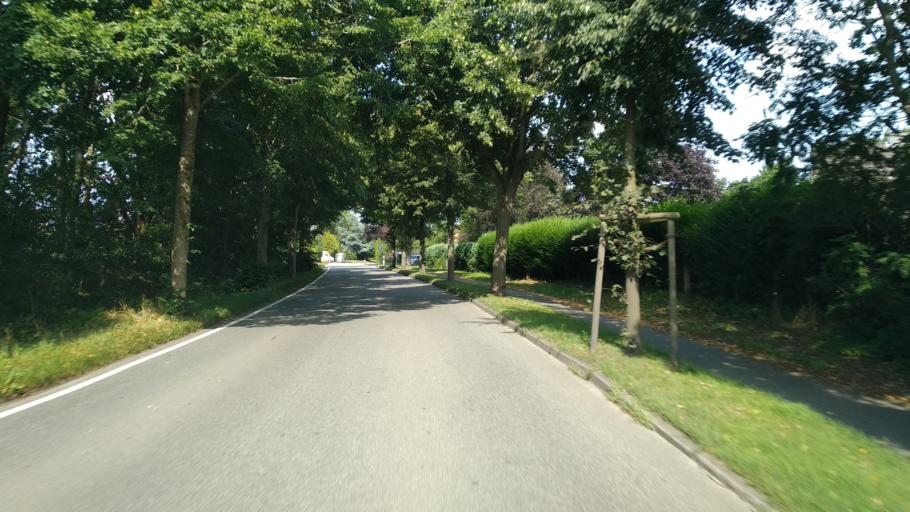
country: DE
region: Schleswig-Holstein
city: Selk
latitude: 54.4692
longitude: 9.5714
